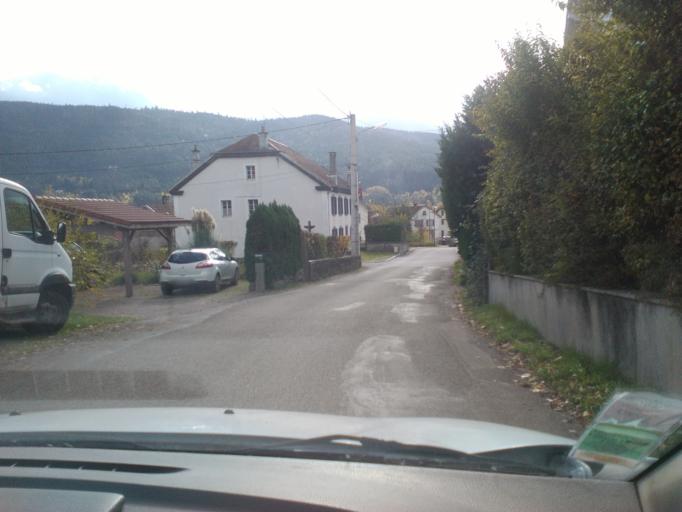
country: FR
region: Lorraine
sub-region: Departement des Vosges
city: Saulxures-sur-Moselotte
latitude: 47.9534
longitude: 6.7799
